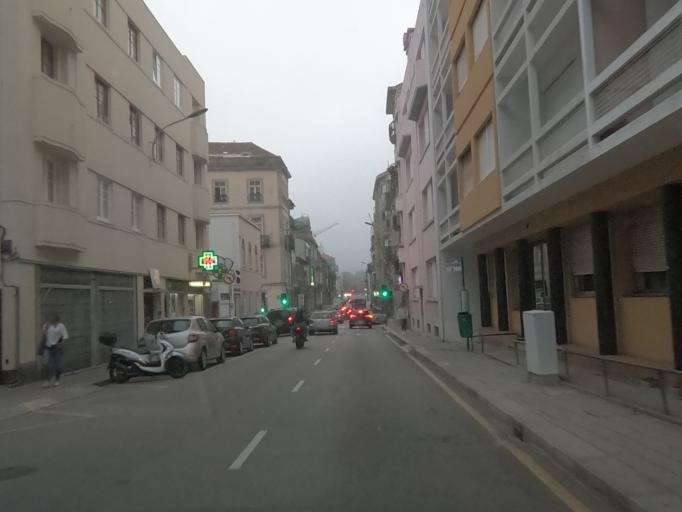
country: PT
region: Porto
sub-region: Porto
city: Porto
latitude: 41.1564
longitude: -8.6201
